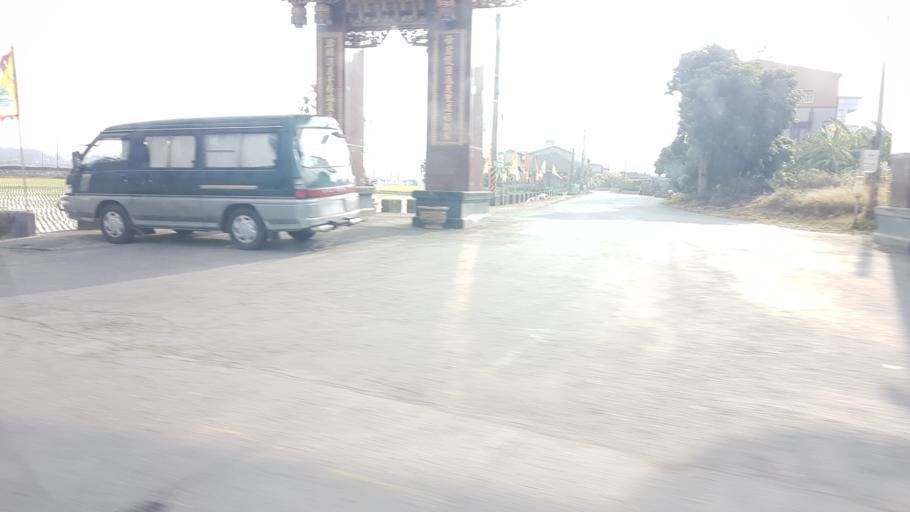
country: TW
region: Taiwan
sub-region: Chiayi
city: Jiayi Shi
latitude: 23.3967
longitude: 120.4285
